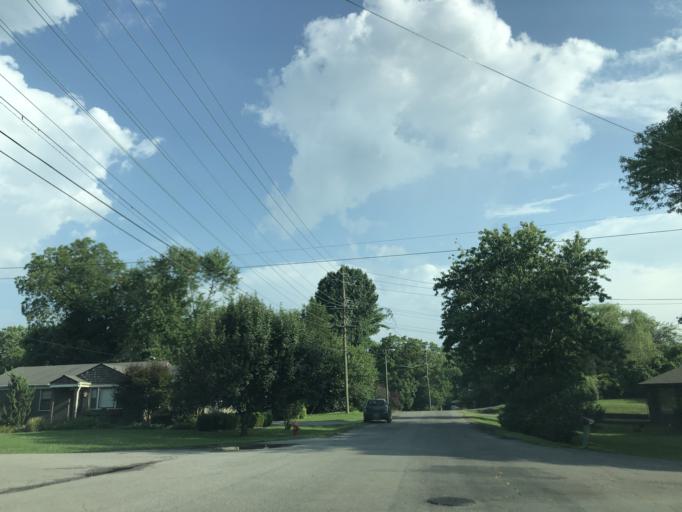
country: US
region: Tennessee
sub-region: Davidson County
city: Lakewood
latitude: 36.1527
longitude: -86.6626
